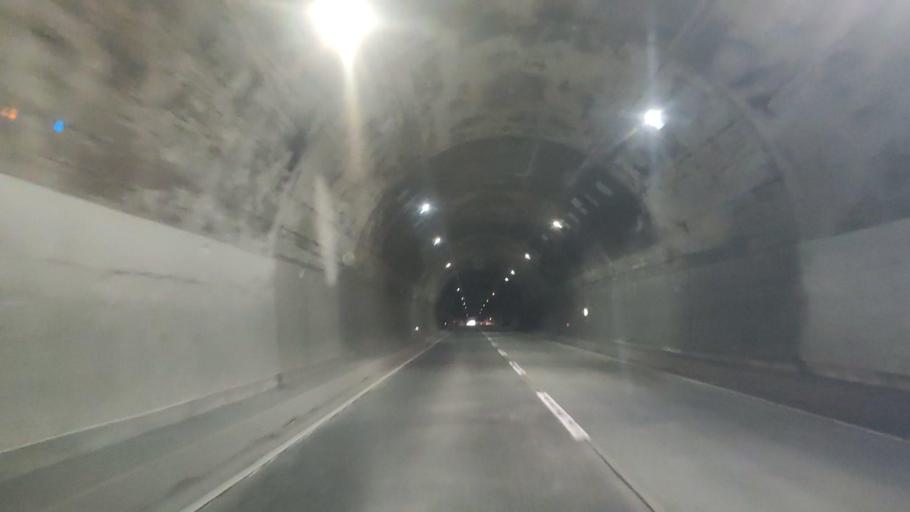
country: JP
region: Kagoshima
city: Okuchi-shinohara
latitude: 31.9760
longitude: 130.7414
